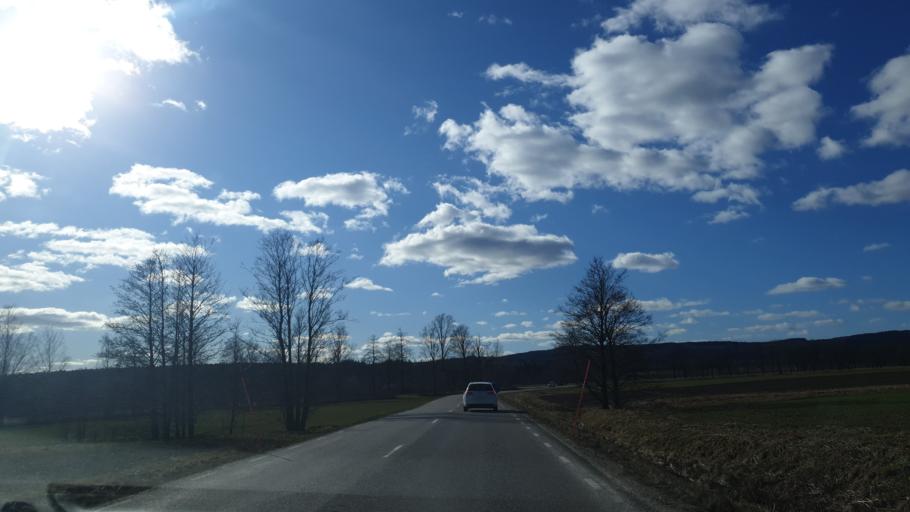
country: SE
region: OErebro
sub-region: Orebro Kommun
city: Garphyttan
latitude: 59.3392
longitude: 15.0338
